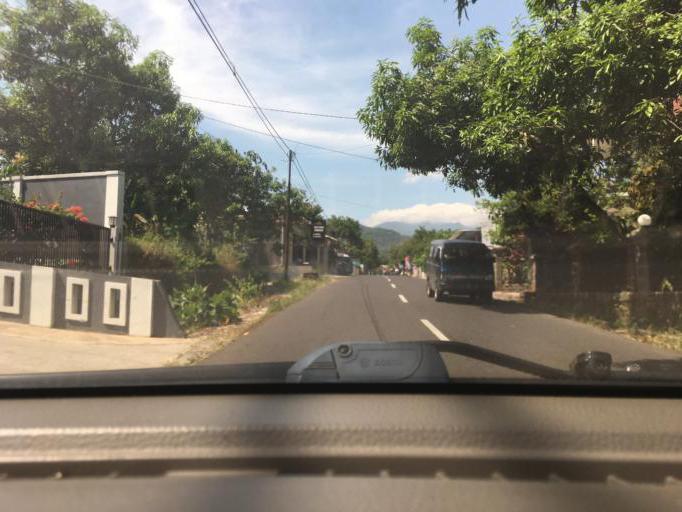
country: ID
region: West Java
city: Cilengkrang
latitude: -6.9509
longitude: 108.0940
